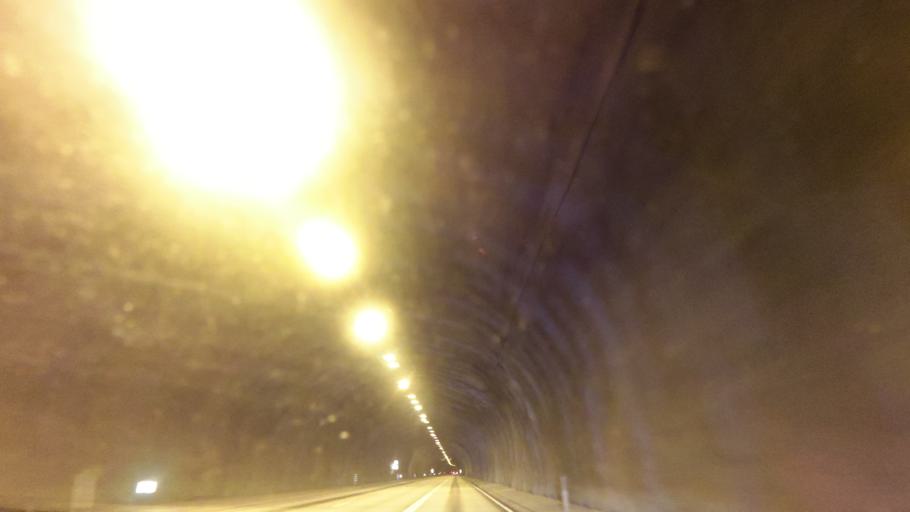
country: IS
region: West
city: Akranes
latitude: 64.3104
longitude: -21.9026
